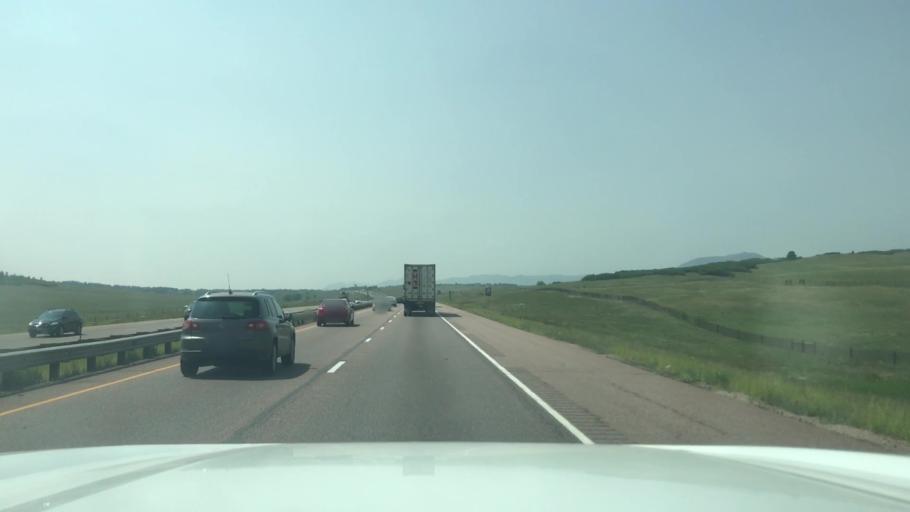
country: US
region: Colorado
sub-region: El Paso County
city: Woodmoor
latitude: 39.1536
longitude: -104.8577
